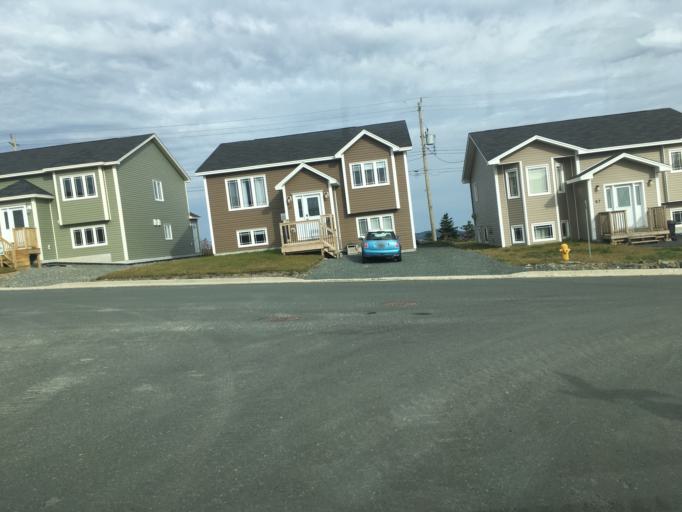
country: CA
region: Newfoundland and Labrador
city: Mount Pearl
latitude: 47.5511
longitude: -52.7840
